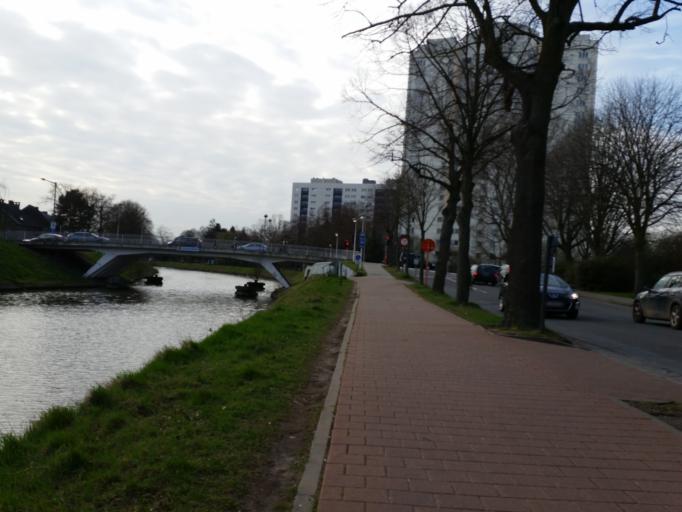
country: BE
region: Flanders
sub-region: Provincie Oost-Vlaanderen
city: Gent
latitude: 51.0440
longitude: 3.7039
